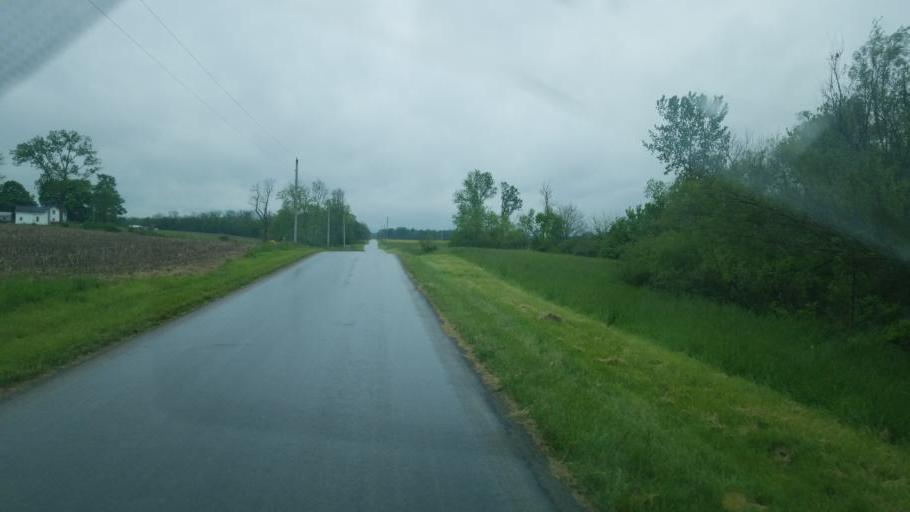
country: US
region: Ohio
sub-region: Highland County
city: Greenfield
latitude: 39.3275
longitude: -83.4284
